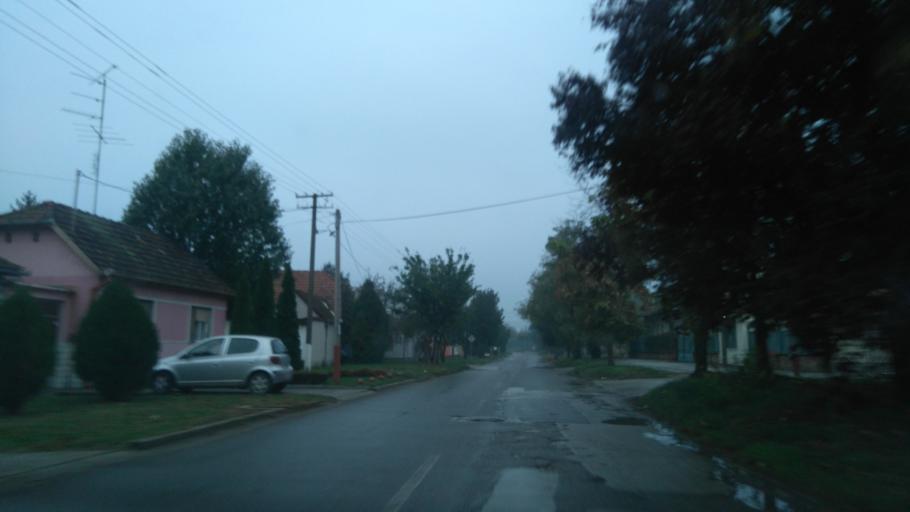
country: RS
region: Autonomna Pokrajina Vojvodina
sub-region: Juznobacki Okrug
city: Becej
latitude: 45.6266
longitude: 20.0380
